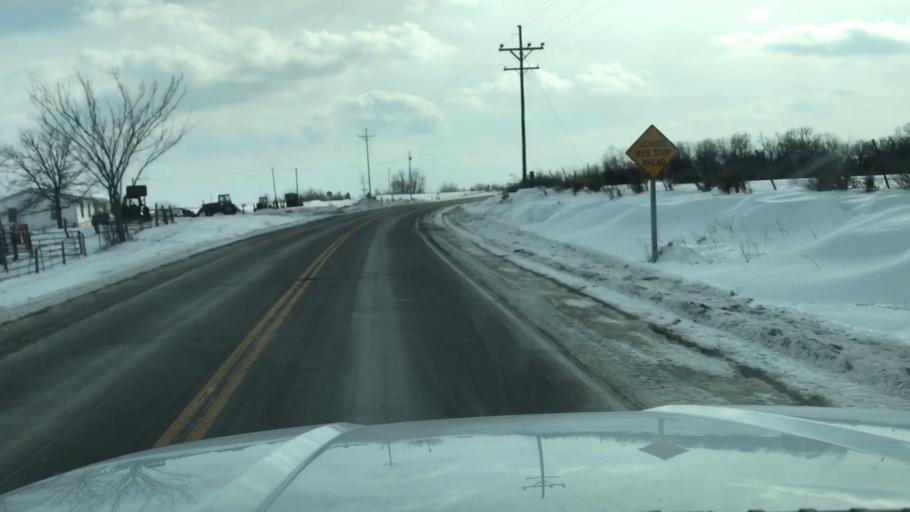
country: US
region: Missouri
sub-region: Gentry County
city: Stanberry
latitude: 40.3697
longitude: -94.6474
